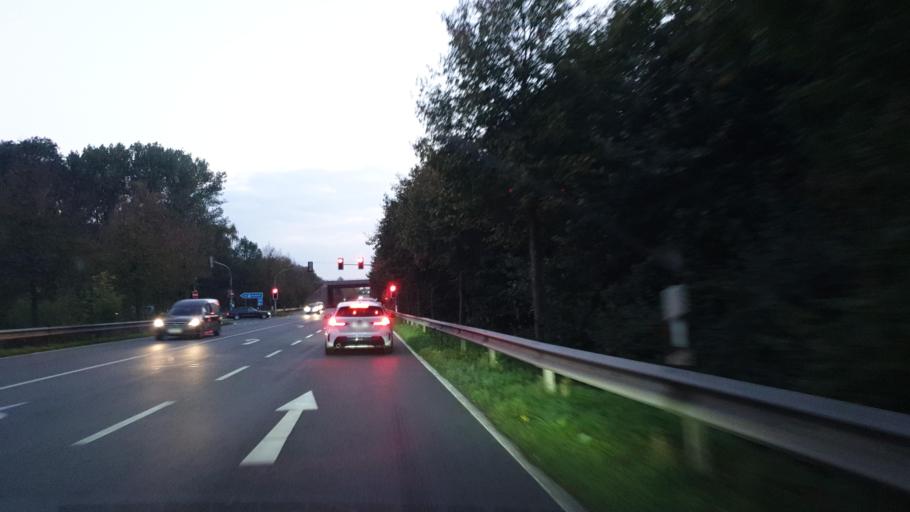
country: DE
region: North Rhine-Westphalia
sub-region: Regierungsbezirk Detmold
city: Kirchlengern
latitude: 52.1906
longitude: 8.6612
